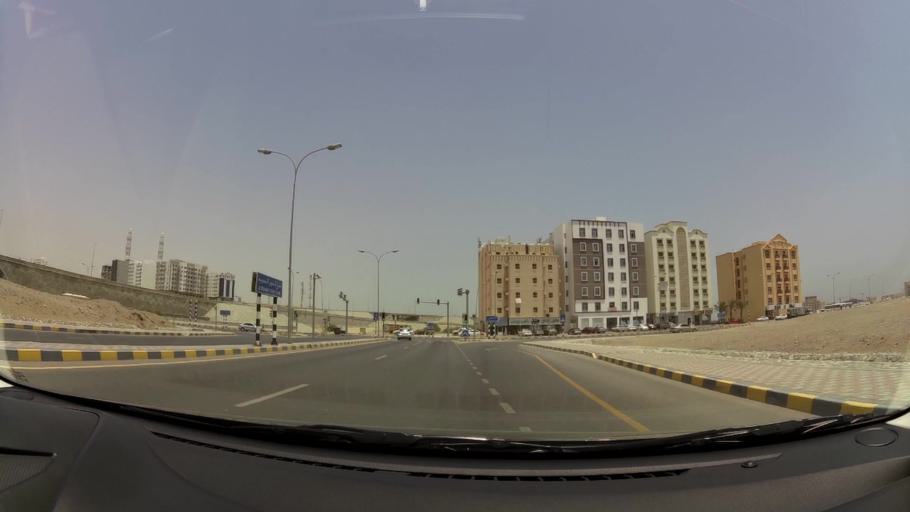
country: OM
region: Muhafazat Masqat
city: Bawshar
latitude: 23.5789
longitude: 58.4207
